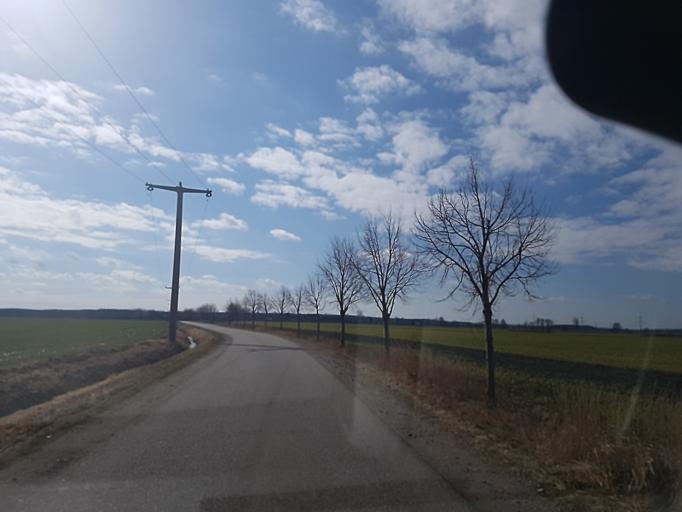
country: DE
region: Brandenburg
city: Ruckersdorf
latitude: 51.5763
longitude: 13.5250
